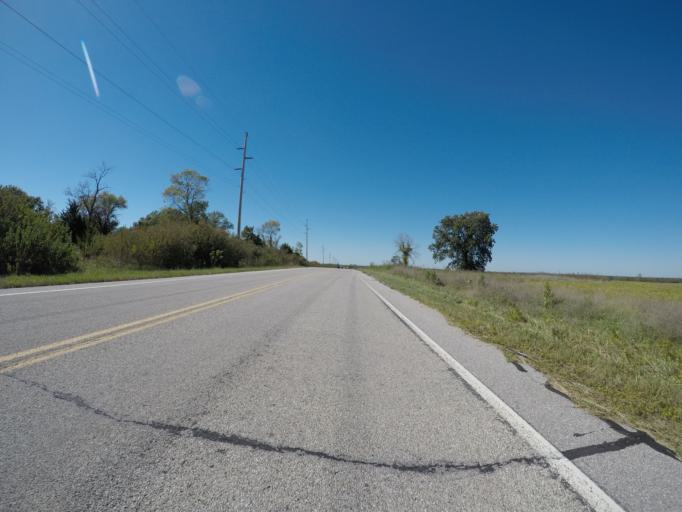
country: US
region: Kansas
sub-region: Douglas County
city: Eudora
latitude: 38.9424
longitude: -95.0285
